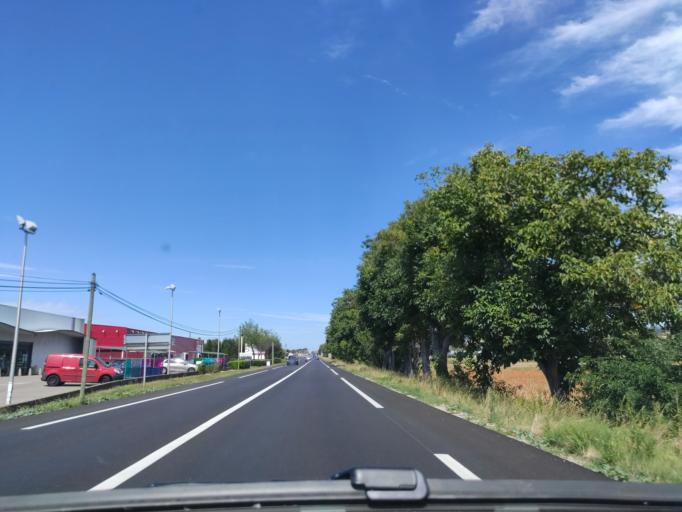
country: FR
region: Rhone-Alpes
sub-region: Departement de l'Isere
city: Reventin-Vaugris
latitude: 45.4521
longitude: 4.8235
